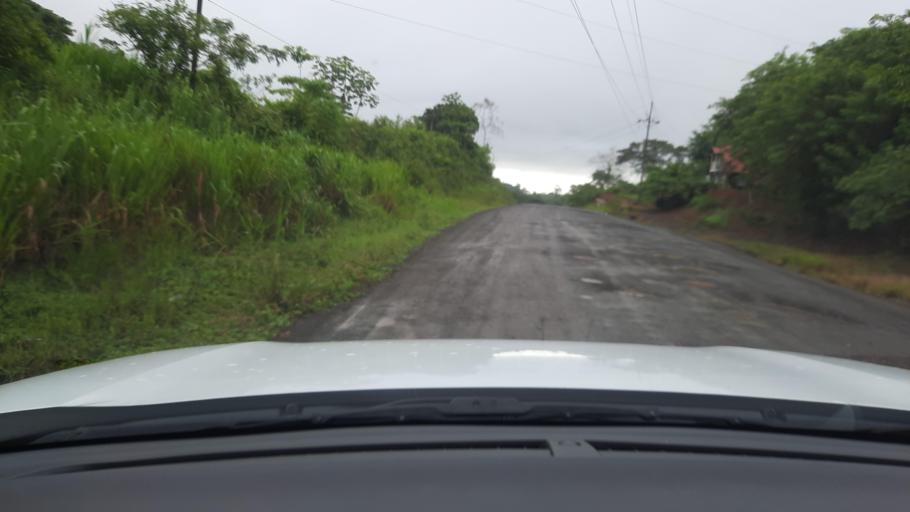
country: CR
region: Alajuela
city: San Jose
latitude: 11.0135
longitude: -85.3381
